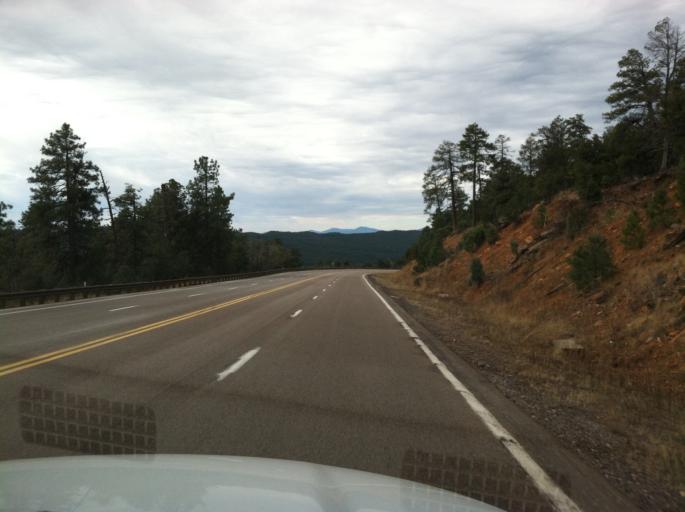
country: US
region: Arizona
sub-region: Gila County
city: Star Valley
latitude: 34.3065
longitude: -110.9351
